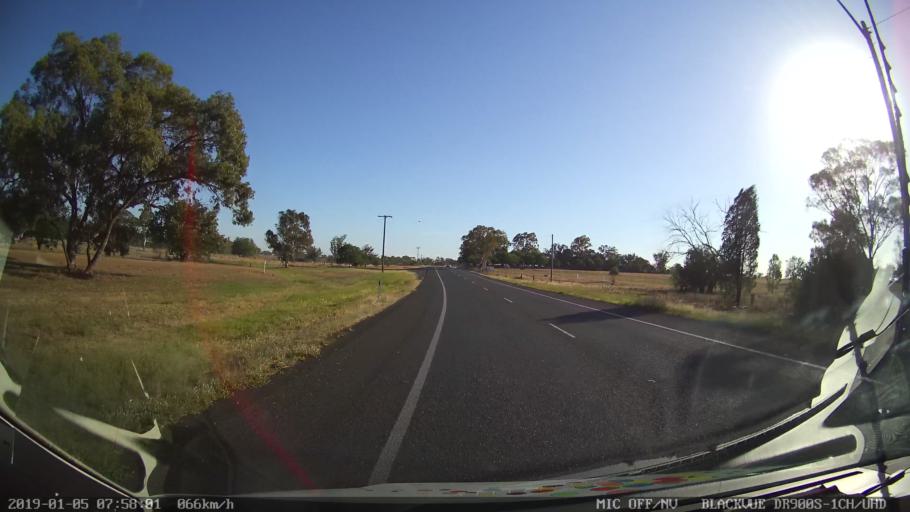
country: AU
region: New South Wales
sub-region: Gilgandra
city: Gilgandra
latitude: -31.7151
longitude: 148.6722
